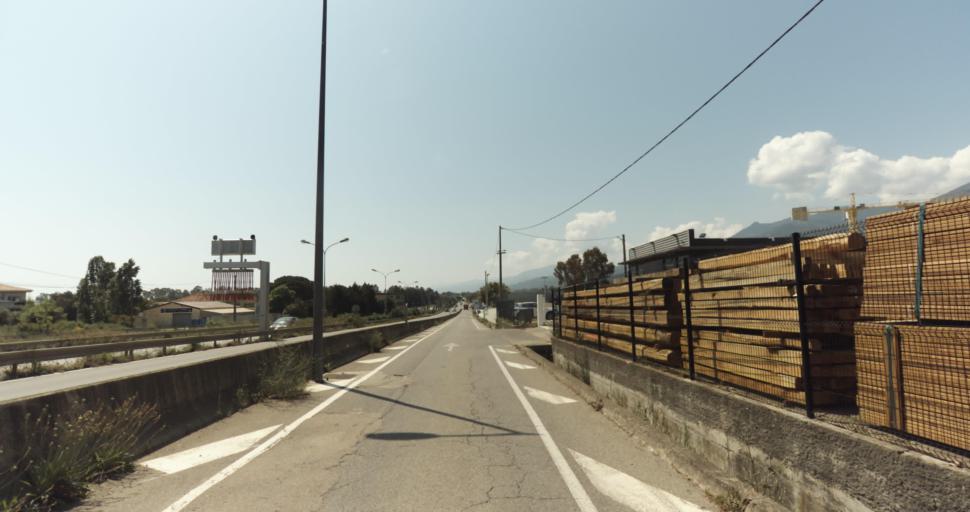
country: FR
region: Corsica
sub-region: Departement de la Haute-Corse
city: Biguglia
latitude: 42.6177
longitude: 9.4371
